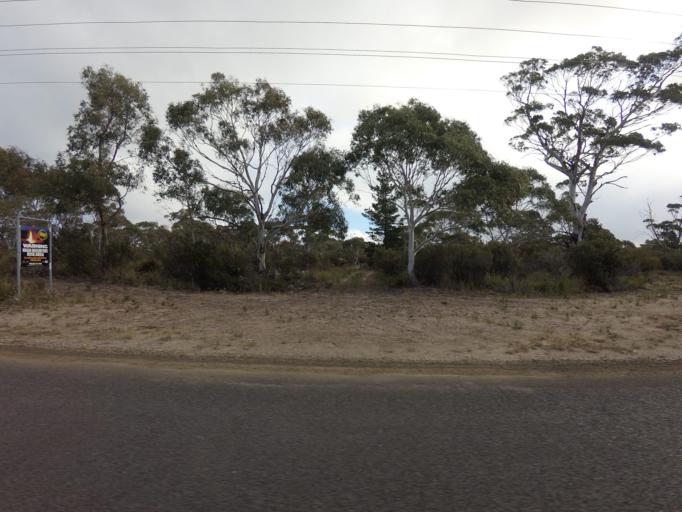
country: AU
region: Tasmania
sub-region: Break O'Day
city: St Helens
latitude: -42.0974
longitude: 148.0867
